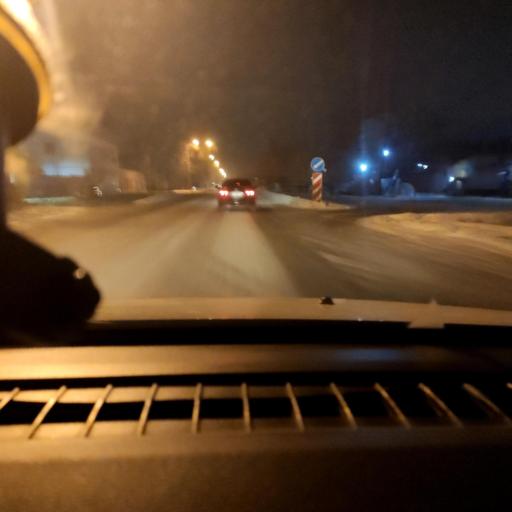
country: RU
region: Samara
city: Samara
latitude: 53.1090
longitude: 50.0698
